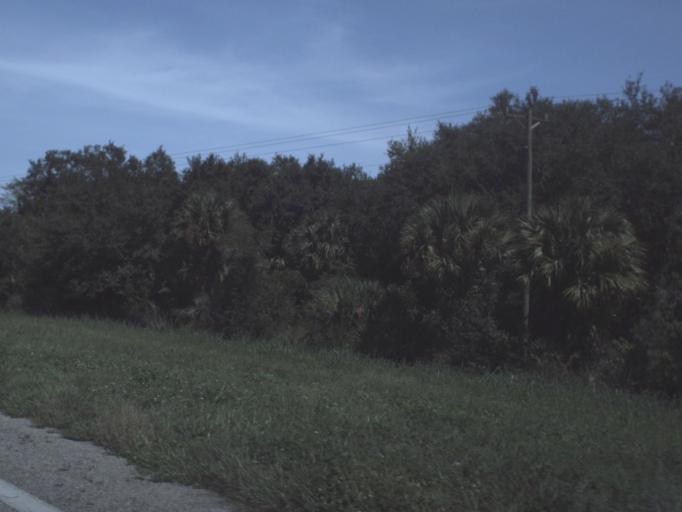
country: US
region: Florida
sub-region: Hendry County
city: Port LaBelle
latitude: 26.9703
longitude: -81.3166
